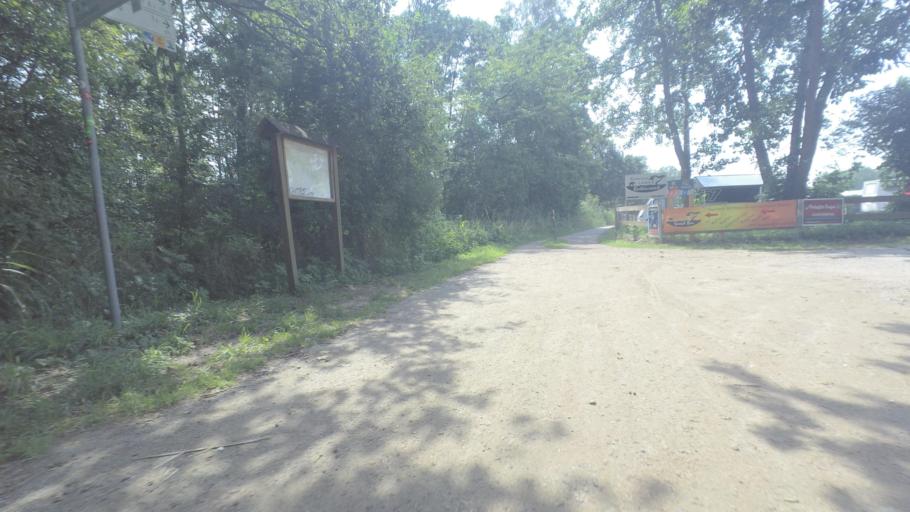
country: DE
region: Mecklenburg-Vorpommern
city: Waren
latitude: 53.5118
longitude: 12.6525
